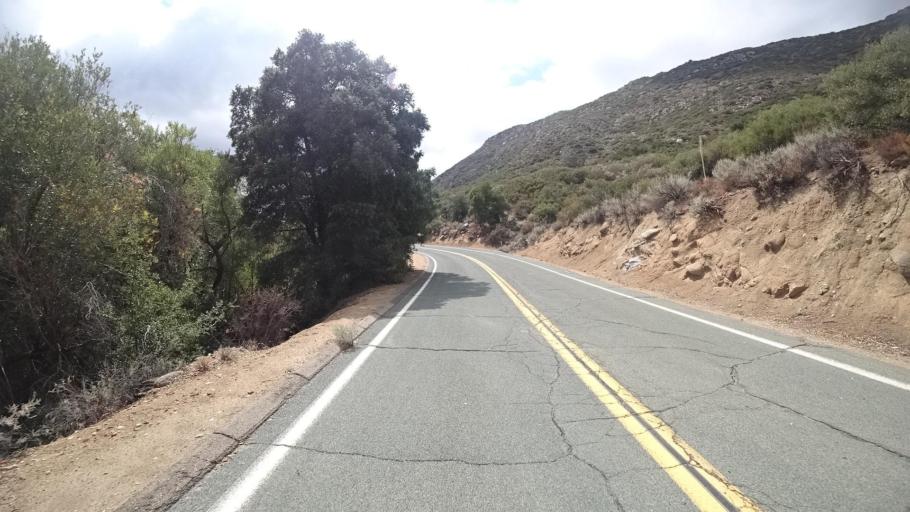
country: US
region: California
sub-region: San Diego County
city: Pine Valley
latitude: 32.7770
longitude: -116.4496
